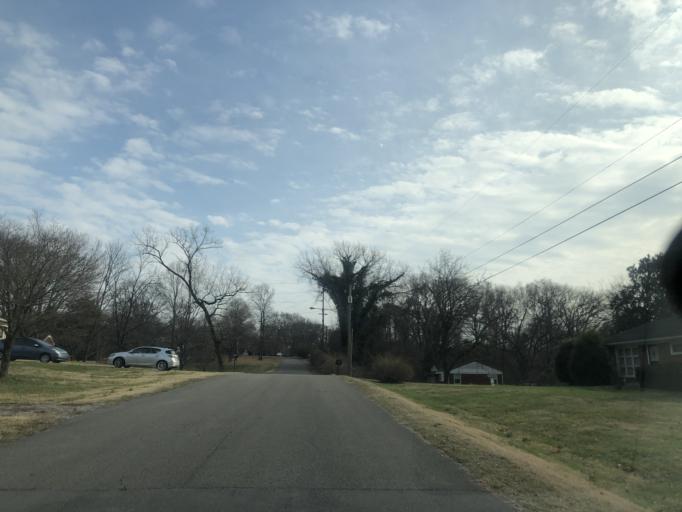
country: US
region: Tennessee
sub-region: Davidson County
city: Oak Hill
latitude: 36.1022
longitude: -86.7064
